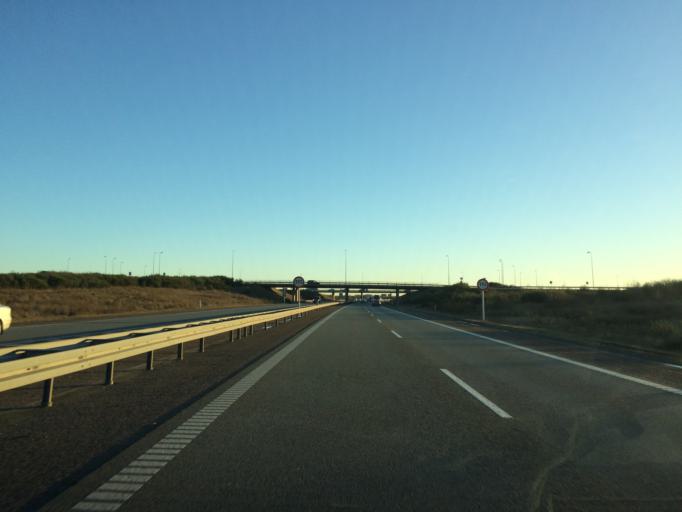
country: DK
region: Central Jutland
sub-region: Herning Kommune
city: Herning
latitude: 56.1581
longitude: 9.0075
